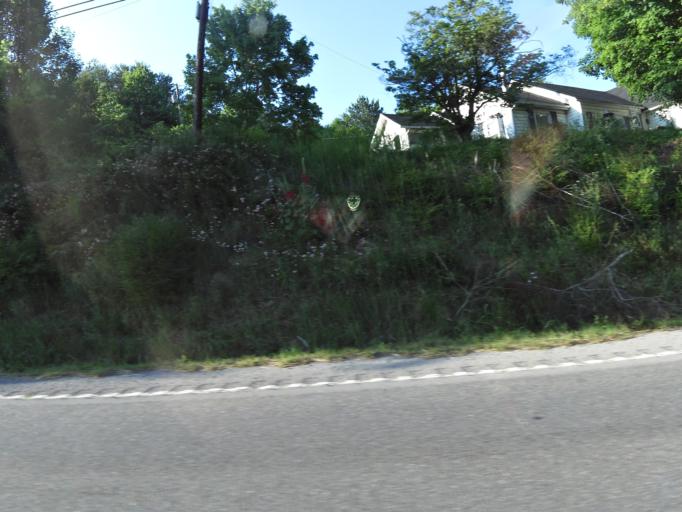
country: US
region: Tennessee
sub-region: Sevier County
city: Seymour
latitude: 35.8578
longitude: -83.6484
